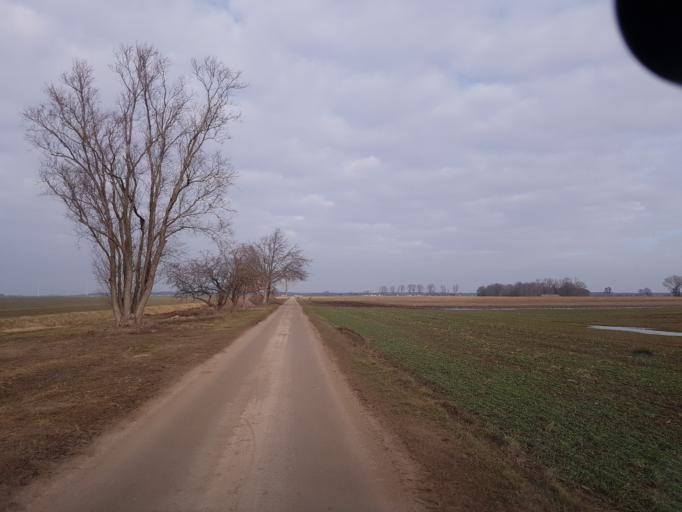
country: DE
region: Brandenburg
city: Doberlug-Kirchhain
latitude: 51.6615
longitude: 13.5432
